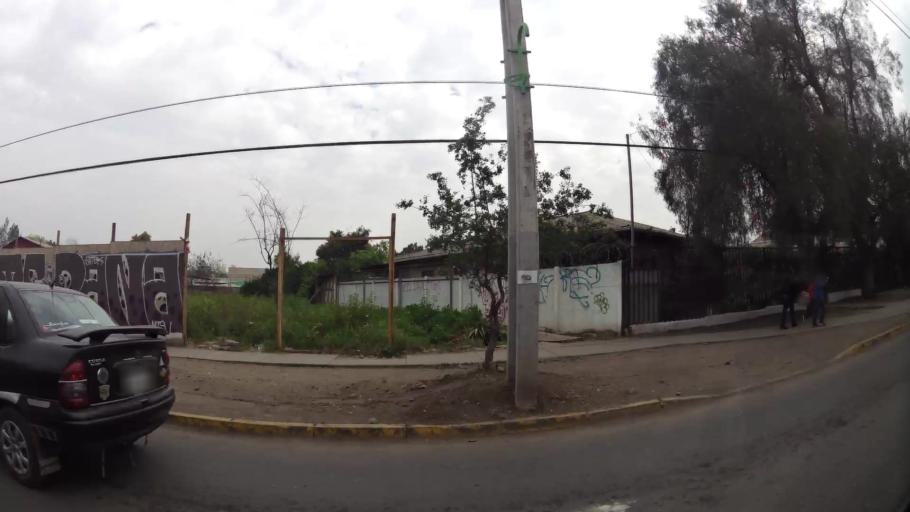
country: CL
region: Santiago Metropolitan
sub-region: Provincia de Chacabuco
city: Chicureo Abajo
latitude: -33.2032
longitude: -70.6800
